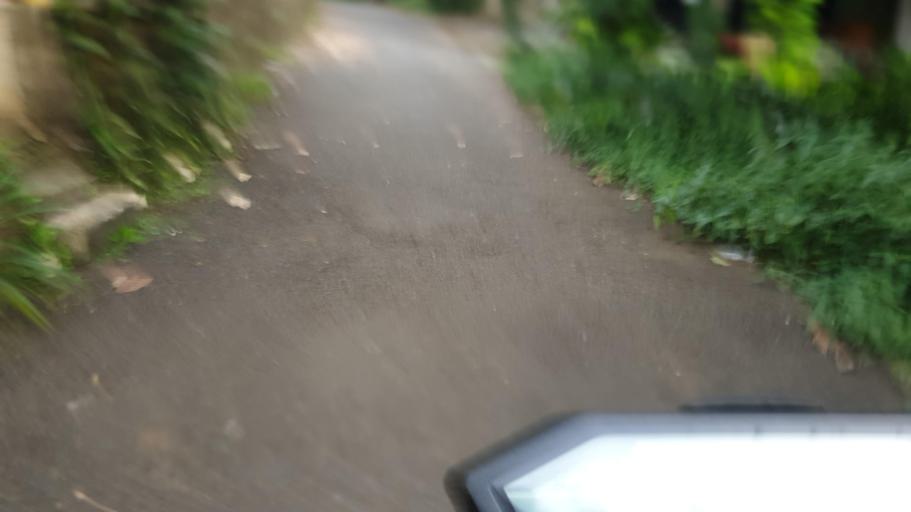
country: ID
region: West Java
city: Depok
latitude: -6.3624
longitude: 106.8390
